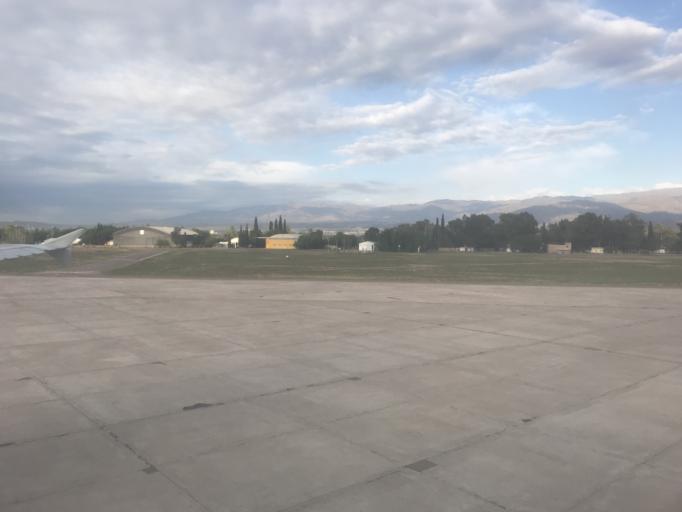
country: AR
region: Mendoza
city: Las Heras
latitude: -32.8430
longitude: -68.7937
